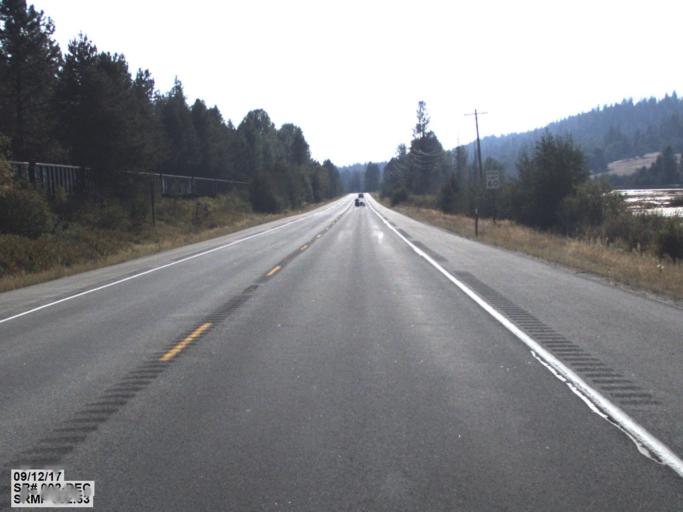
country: US
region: Washington
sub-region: Pend Oreille County
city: Newport
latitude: 48.1717
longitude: -117.0708
